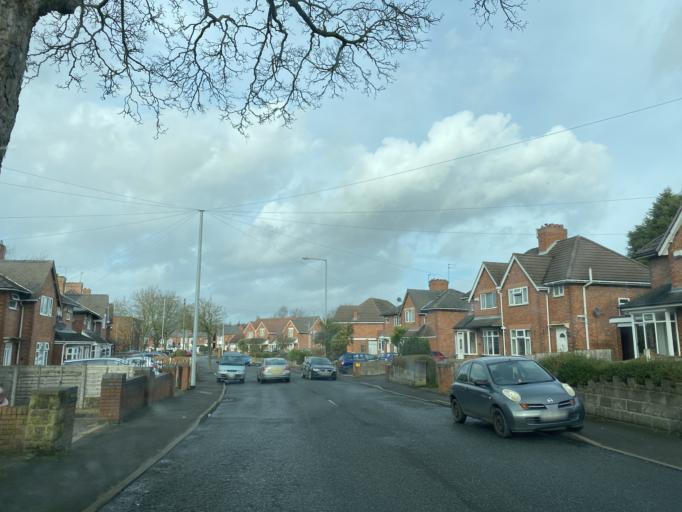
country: GB
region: England
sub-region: Walsall
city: Walsall
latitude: 52.5855
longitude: -2.0020
